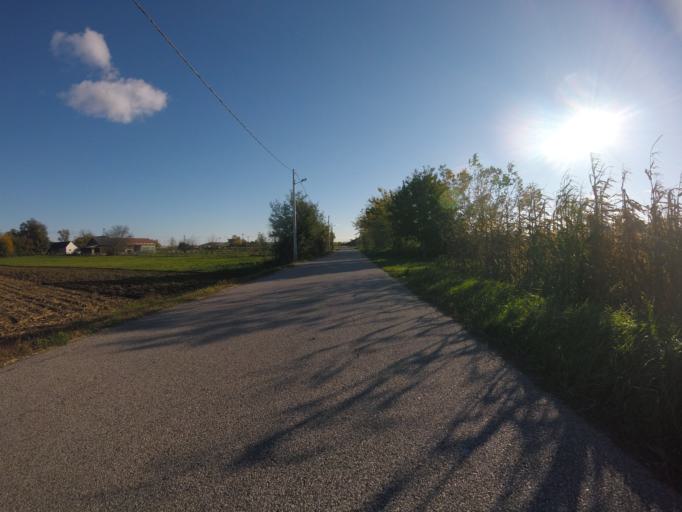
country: HR
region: Grad Zagreb
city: Odra
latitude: 45.7535
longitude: 16.0002
